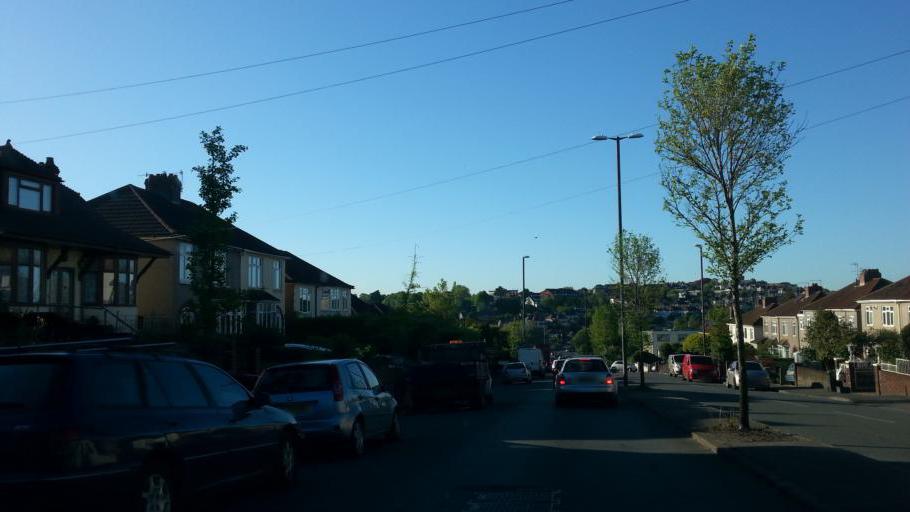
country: GB
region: England
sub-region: Bath and North East Somerset
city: Whitchurch
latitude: 51.4243
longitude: -2.5629
